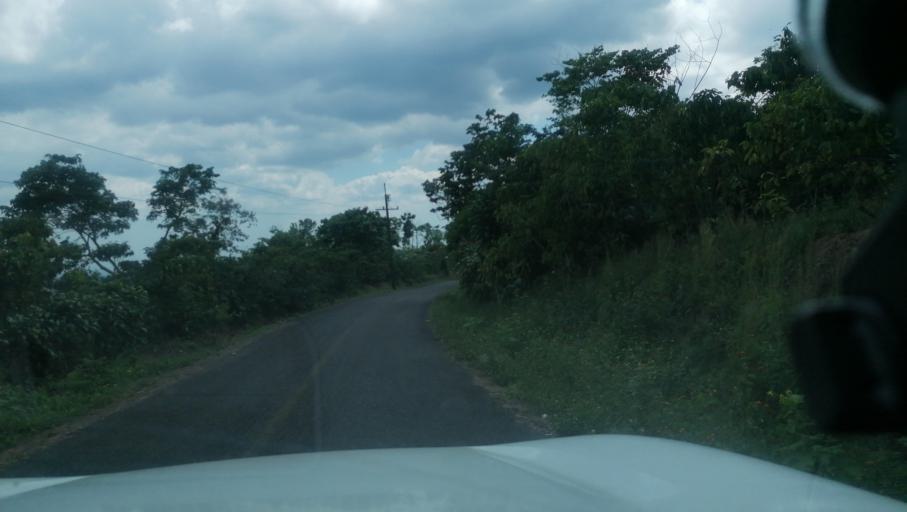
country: MX
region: Chiapas
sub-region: Cacahoatan
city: Benito Juarez
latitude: 15.0558
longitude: -92.1514
